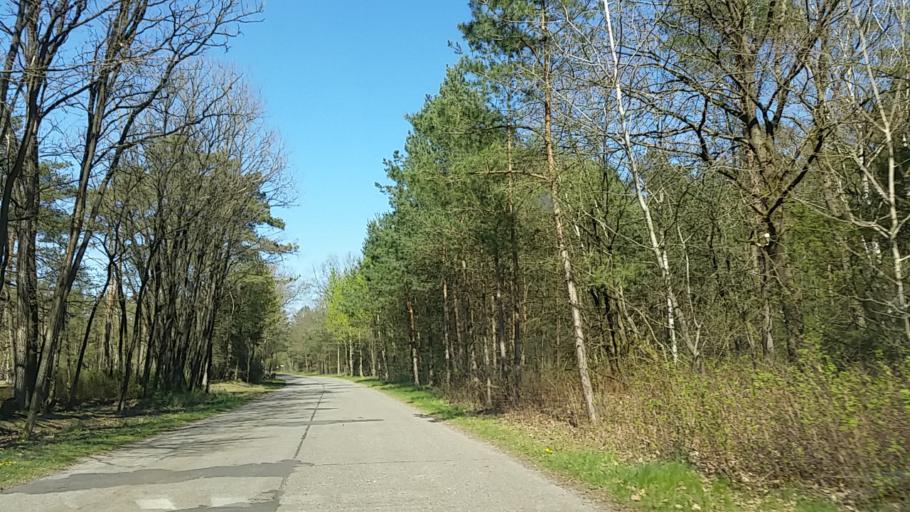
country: DE
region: Lower Saxony
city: Schneverdingen
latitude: 53.1546
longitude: 9.8317
